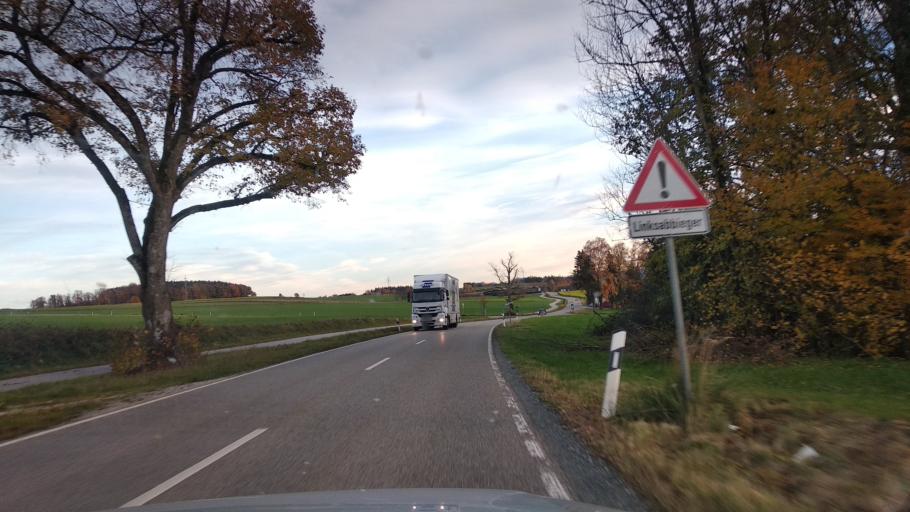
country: DE
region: Bavaria
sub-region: Upper Bavaria
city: Grafing bei Munchen
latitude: 48.0329
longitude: 11.9835
